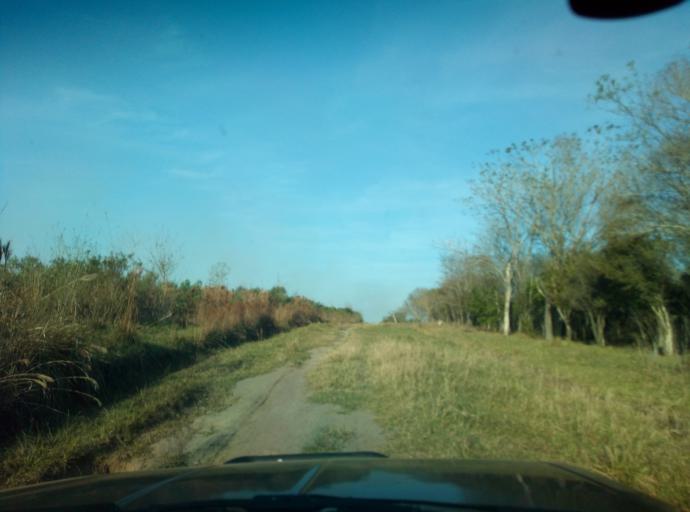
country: PY
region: Caaguazu
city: Doctor Cecilio Baez
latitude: -25.1999
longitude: -56.1236
